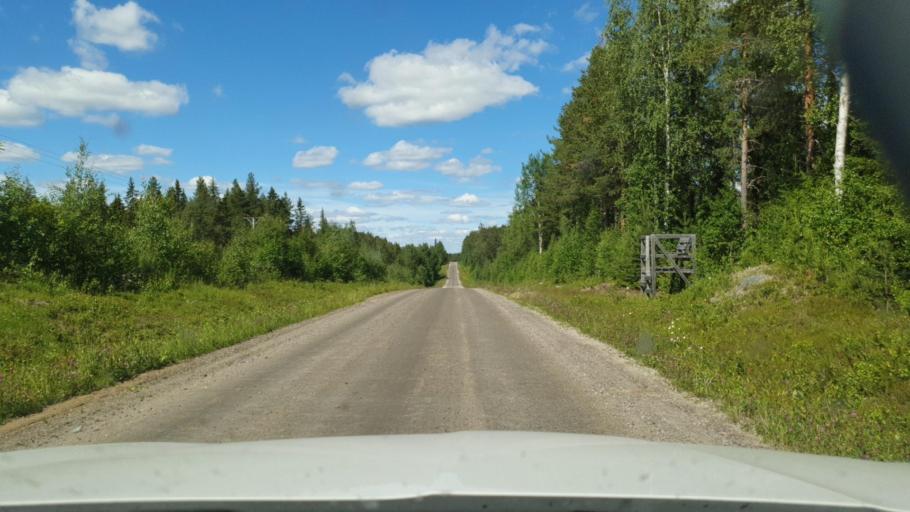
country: SE
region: Vaesterbotten
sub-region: Skelleftea Kommun
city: Byske
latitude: 65.1415
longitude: 21.1784
